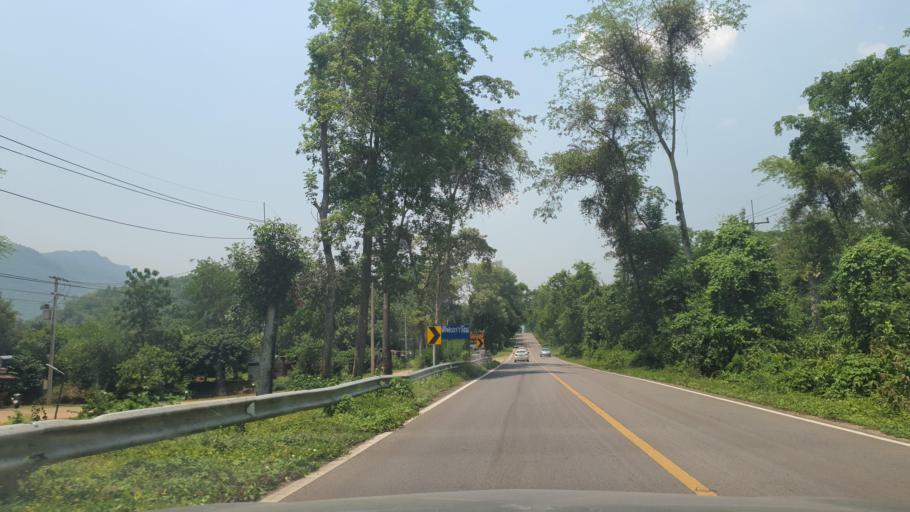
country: TH
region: Kanchanaburi
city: Sai Yok
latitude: 14.2794
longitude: 99.2240
